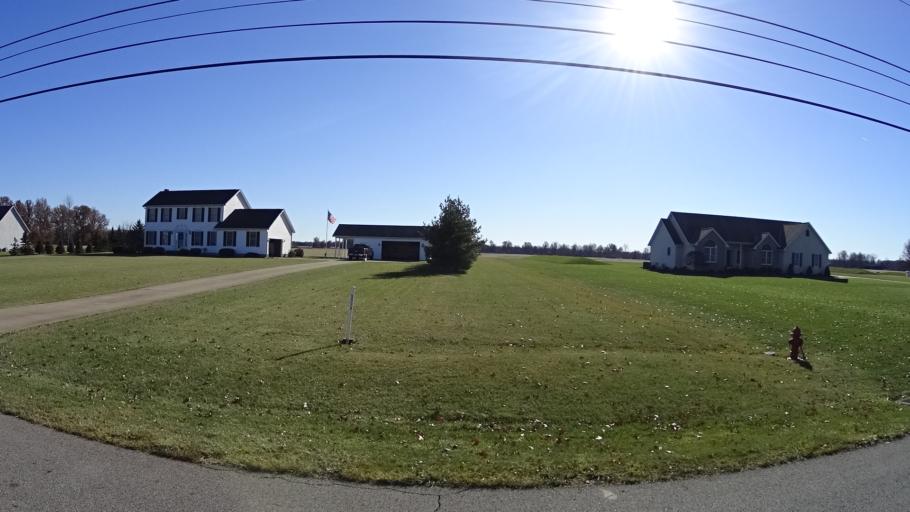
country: US
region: Ohio
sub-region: Lorain County
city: Grafton
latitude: 41.3003
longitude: -82.1111
